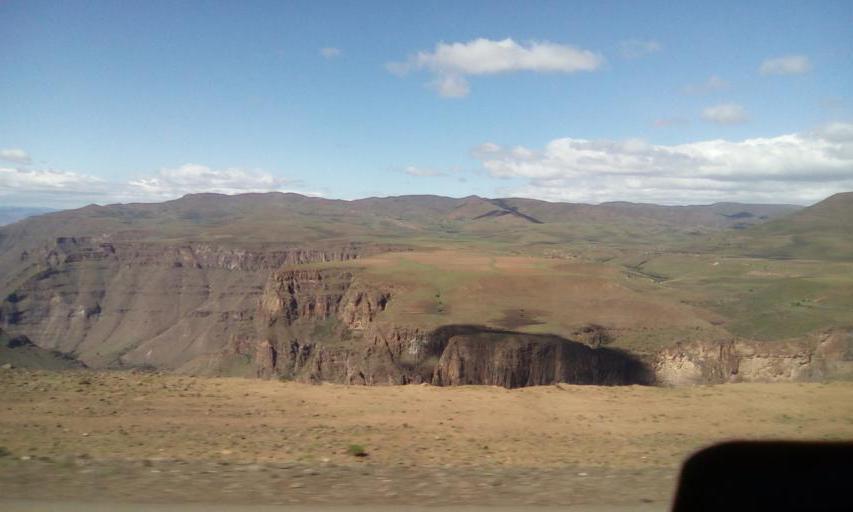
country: LS
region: Maseru
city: Nako
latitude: -29.8757
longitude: 28.0735
